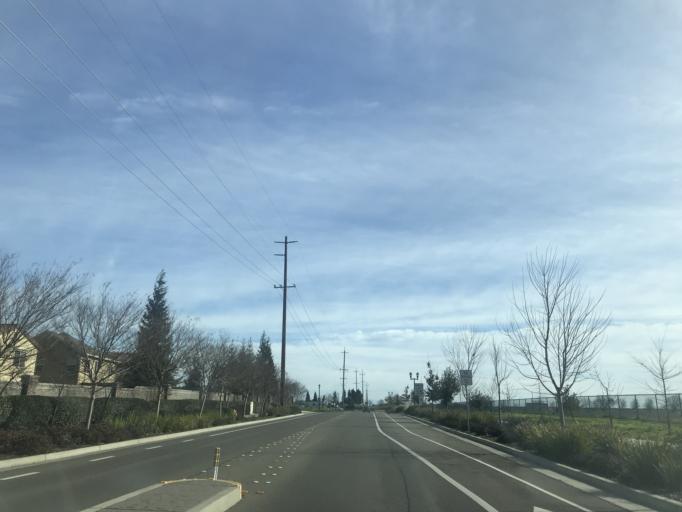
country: US
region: California
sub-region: Yolo County
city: Woodland
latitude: 38.6556
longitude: -121.7590
